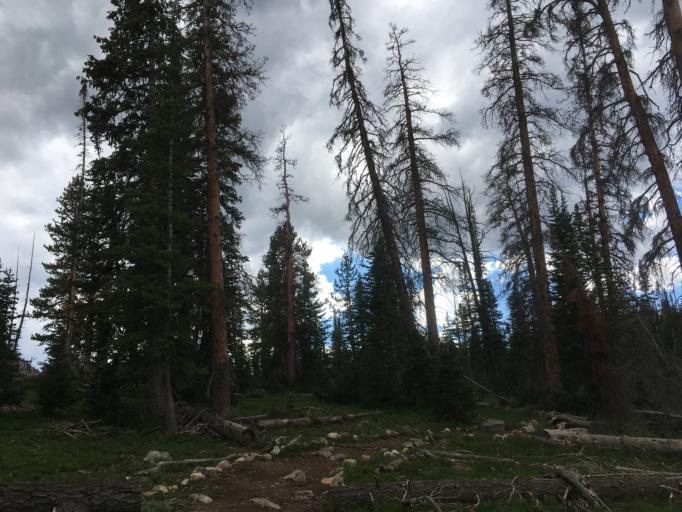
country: US
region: Utah
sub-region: Summit County
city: Kamas
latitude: 40.7167
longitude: -110.8813
